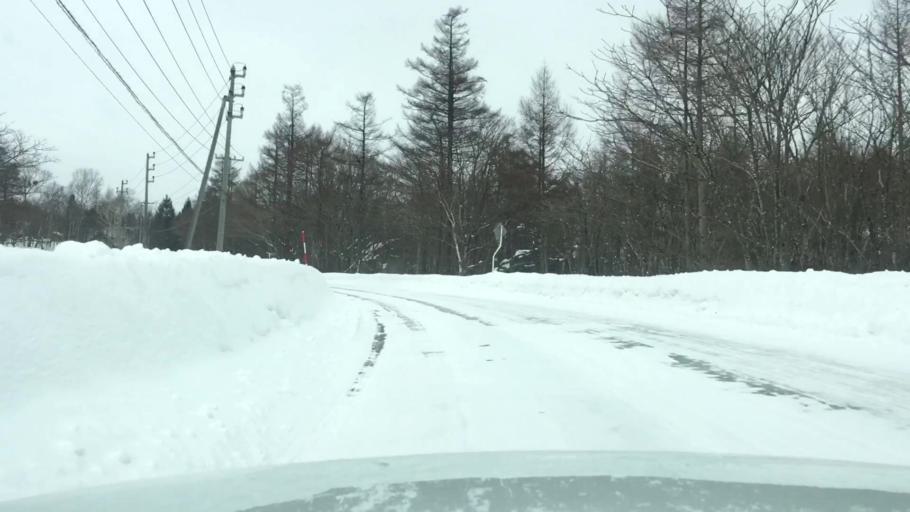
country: JP
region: Akita
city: Hanawa
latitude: 40.0025
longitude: 140.9846
